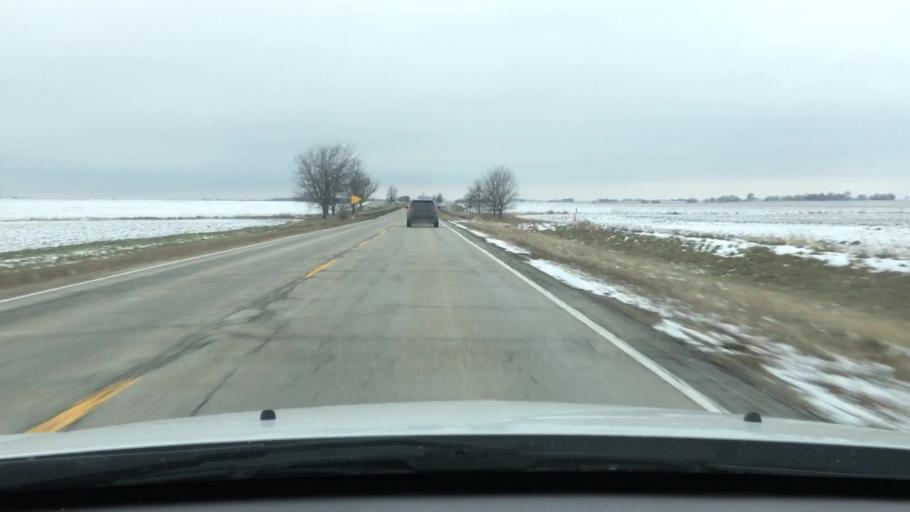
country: US
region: Illinois
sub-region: DeKalb County
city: Malta
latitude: 41.9356
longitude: -88.8978
